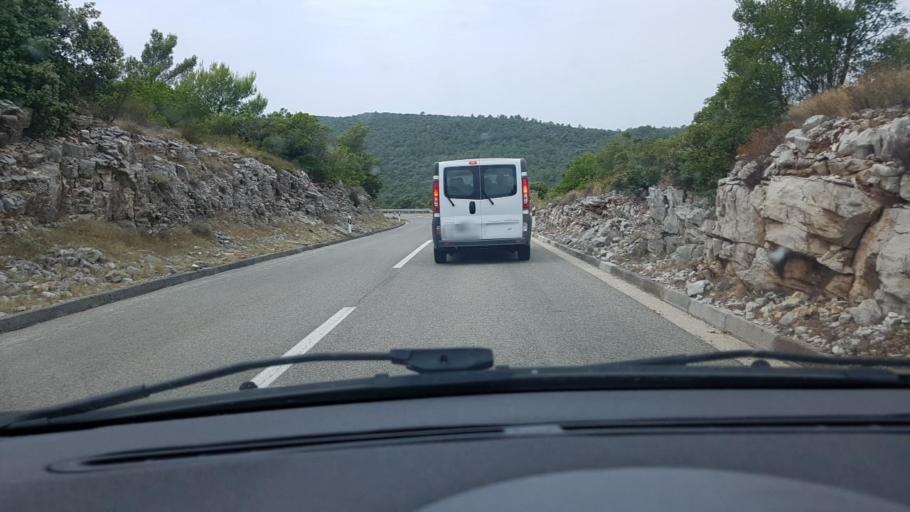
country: HR
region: Dubrovacko-Neretvanska
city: Smokvica
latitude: 42.9493
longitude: 16.9722
